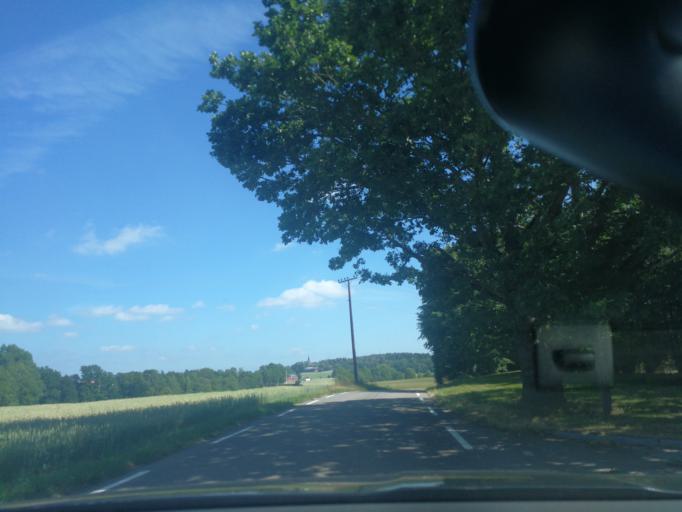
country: NO
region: Vestfold
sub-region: Stokke
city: Stokke
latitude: 59.2106
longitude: 10.2871
